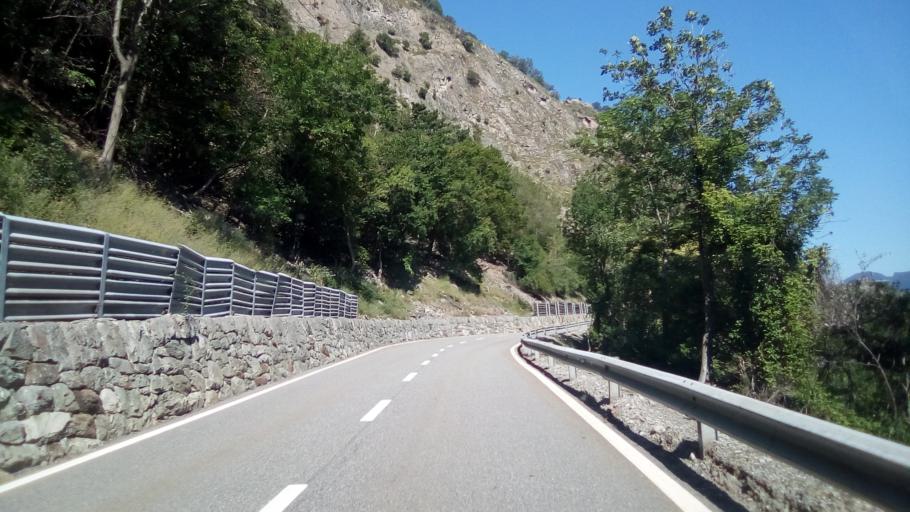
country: CH
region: Valais
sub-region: Saint-Maurice District
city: Vernayaz
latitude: 46.1196
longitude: 7.0437
